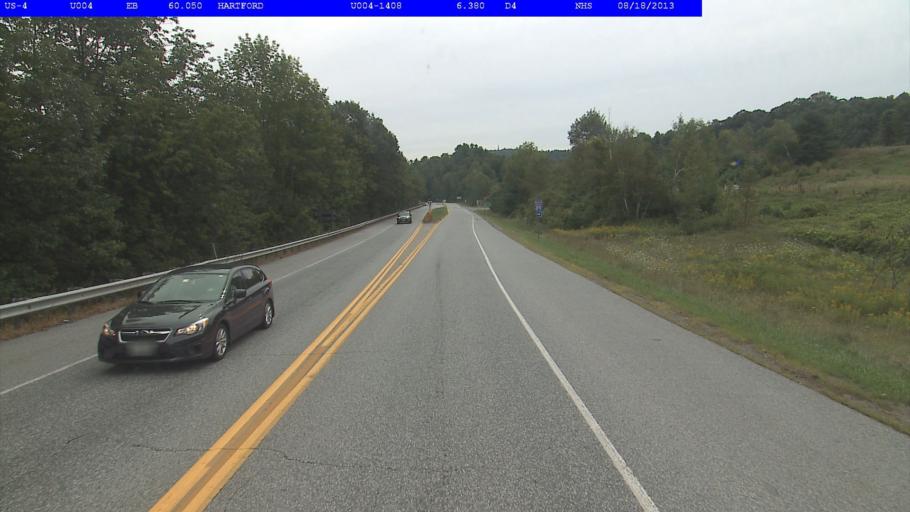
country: US
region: Vermont
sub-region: Windsor County
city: White River Junction
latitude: 43.6666
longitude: -72.3837
